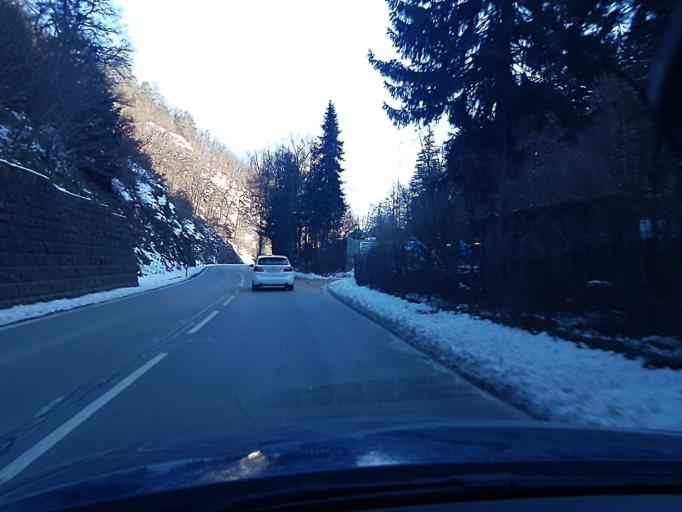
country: DE
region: Baden-Wuerttemberg
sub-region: Freiburg Region
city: Schramberg
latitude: 48.2399
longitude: 8.3747
